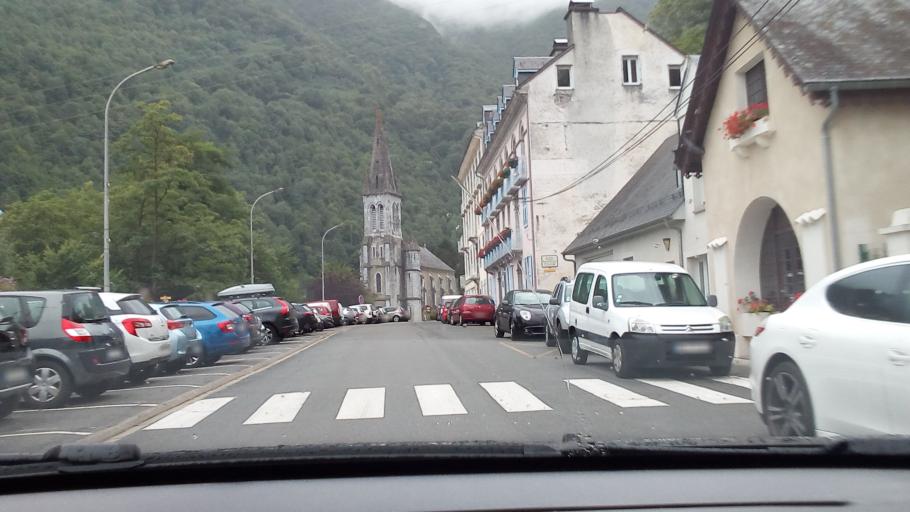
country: FR
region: Midi-Pyrenees
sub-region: Departement des Hautes-Pyrenees
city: Luz-Saint-Sauveur
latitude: 42.8627
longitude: -0.0101
